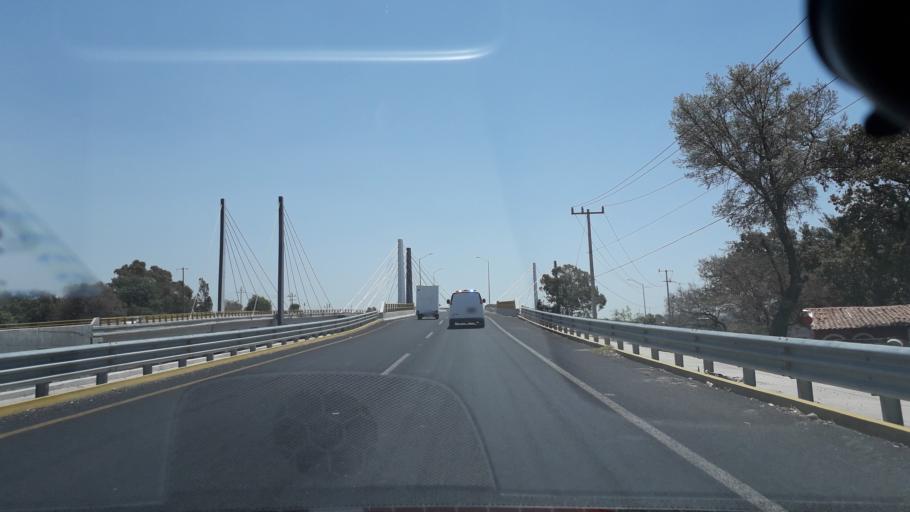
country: MX
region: Puebla
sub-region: Puebla
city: Primero de Mayo
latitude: 19.0655
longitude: -98.1098
